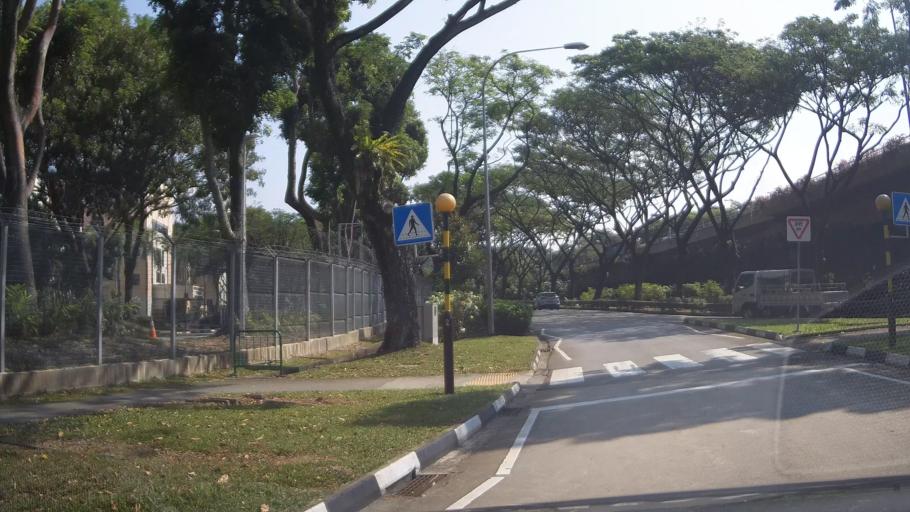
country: MY
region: Johor
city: Johor Bahru
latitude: 1.3313
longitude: 103.6746
